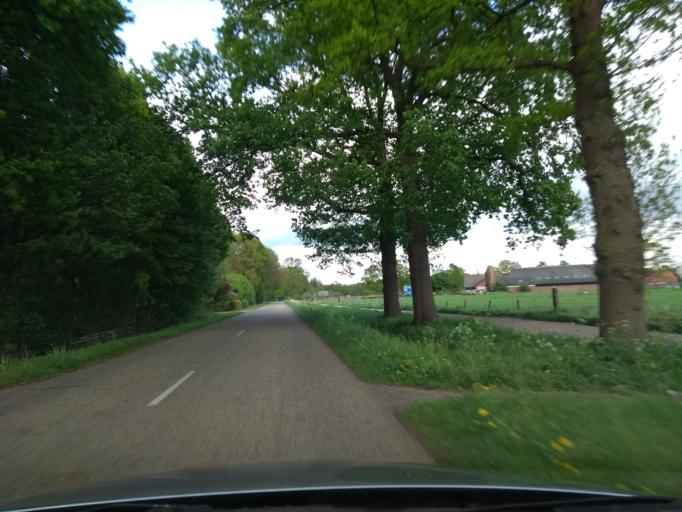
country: NL
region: Gelderland
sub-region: Gemeente Lochem
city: Barchem
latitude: 52.0750
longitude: 6.4078
